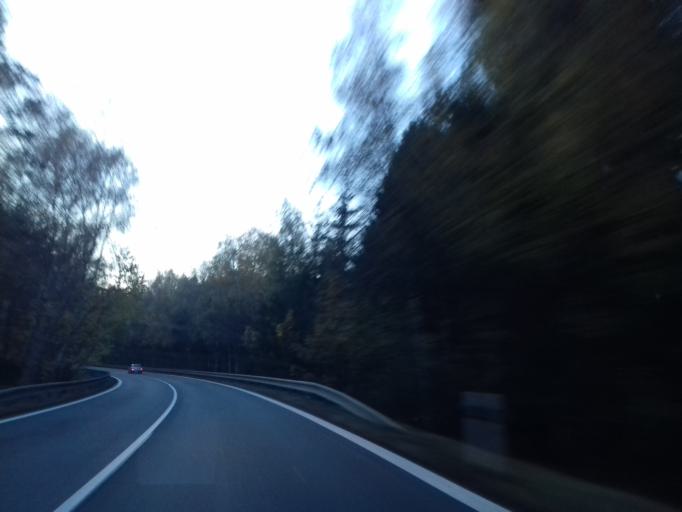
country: CZ
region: Vysocina
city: Chotebor
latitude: 49.6578
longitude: 15.7089
